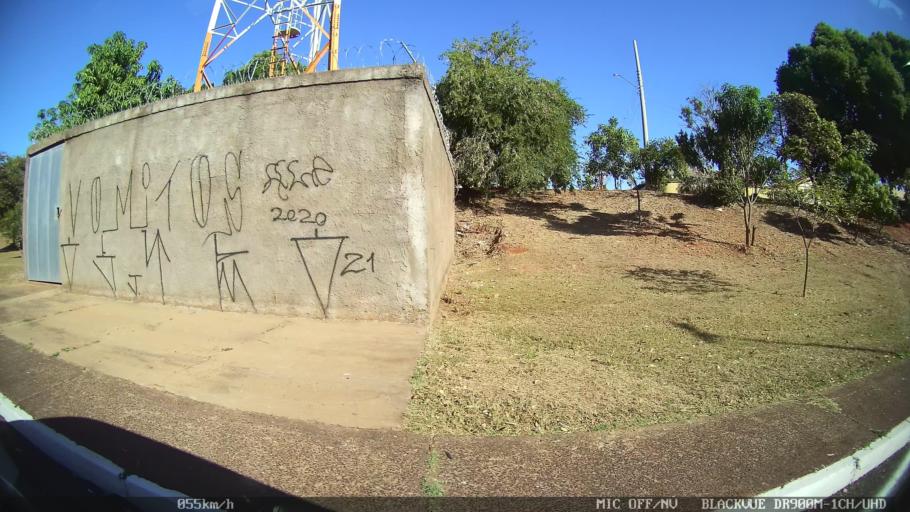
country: BR
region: Sao Paulo
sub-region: Olimpia
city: Olimpia
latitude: -20.7385
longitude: -48.8963
